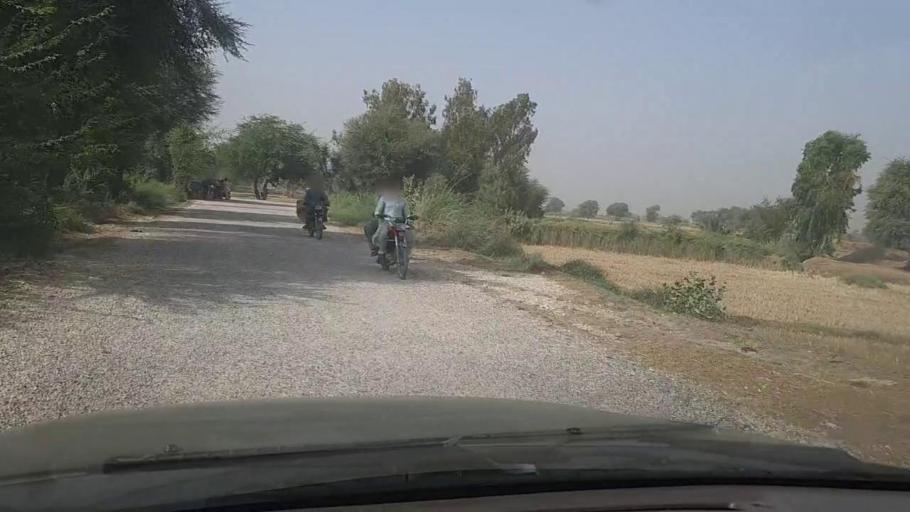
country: PK
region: Sindh
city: Shikarpur
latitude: 27.9126
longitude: 68.6052
